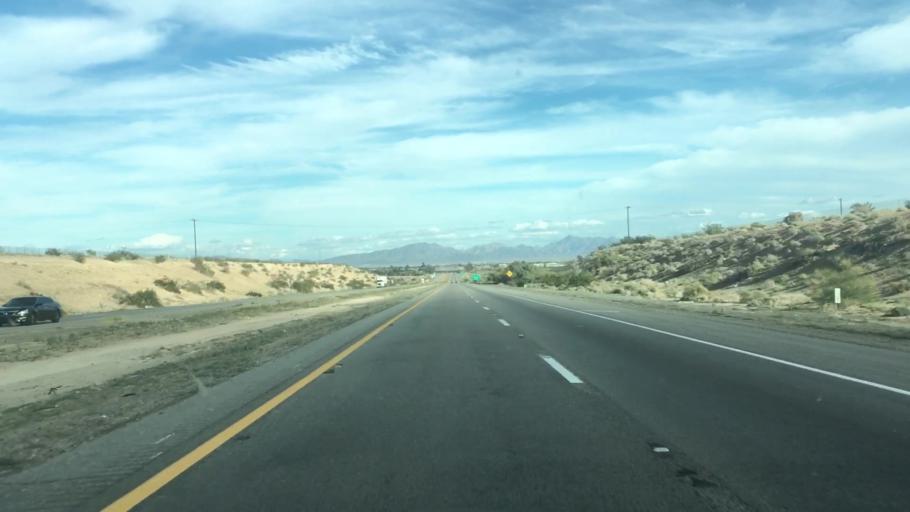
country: US
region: California
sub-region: Riverside County
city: Mesa Verde
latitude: 33.6065
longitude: -114.6777
